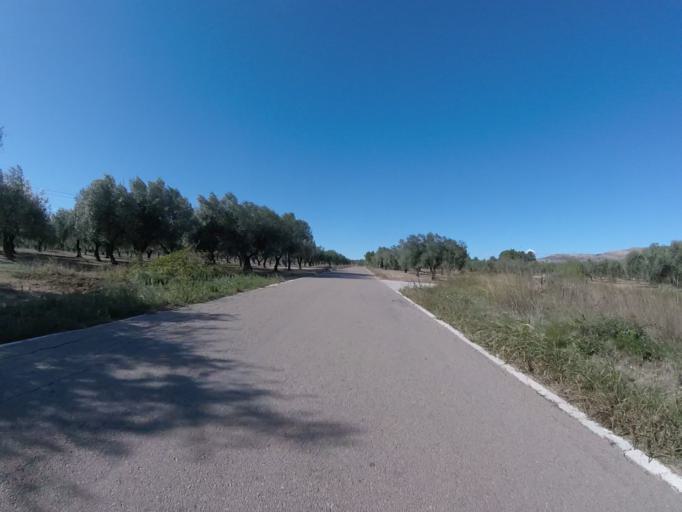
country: ES
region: Valencia
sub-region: Provincia de Castello
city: Chert/Xert
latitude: 40.4604
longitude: 0.1562
